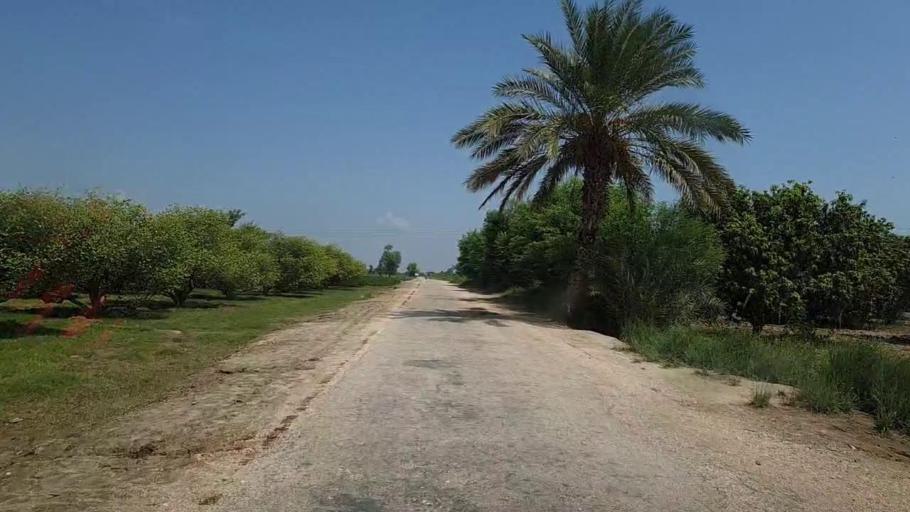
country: PK
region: Sindh
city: Bhiria
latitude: 26.8940
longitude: 68.2231
